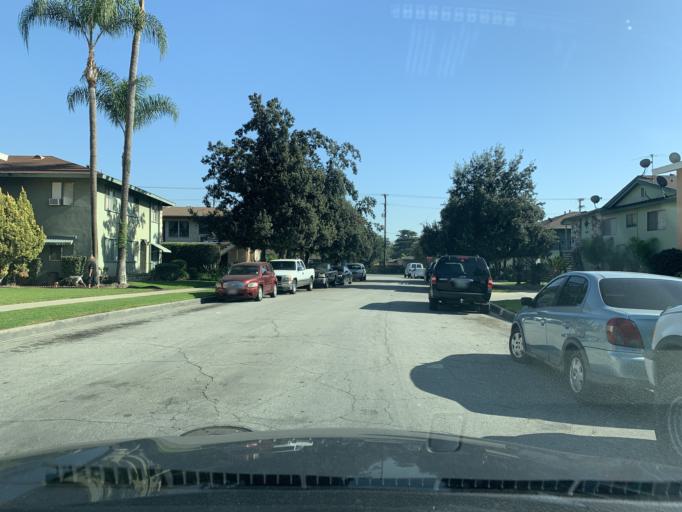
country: US
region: California
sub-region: Los Angeles County
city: Covina
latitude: 34.0849
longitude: -117.8824
